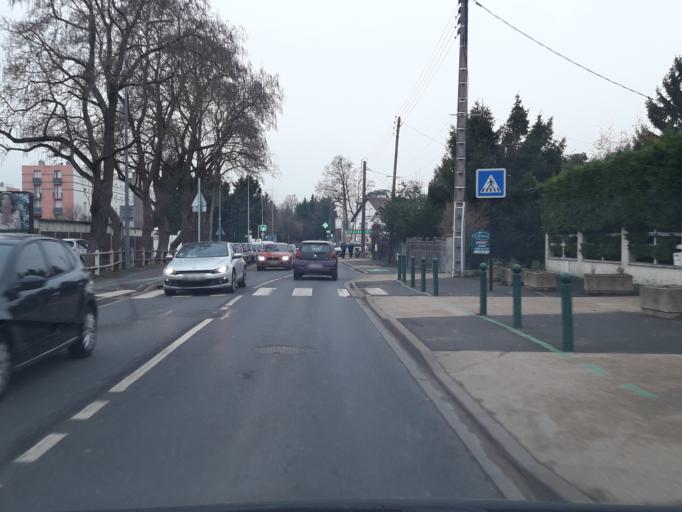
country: FR
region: Ile-de-France
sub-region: Departement de l'Essonne
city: Sainte-Genevieve-des-Bois
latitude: 48.6313
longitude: 2.3379
